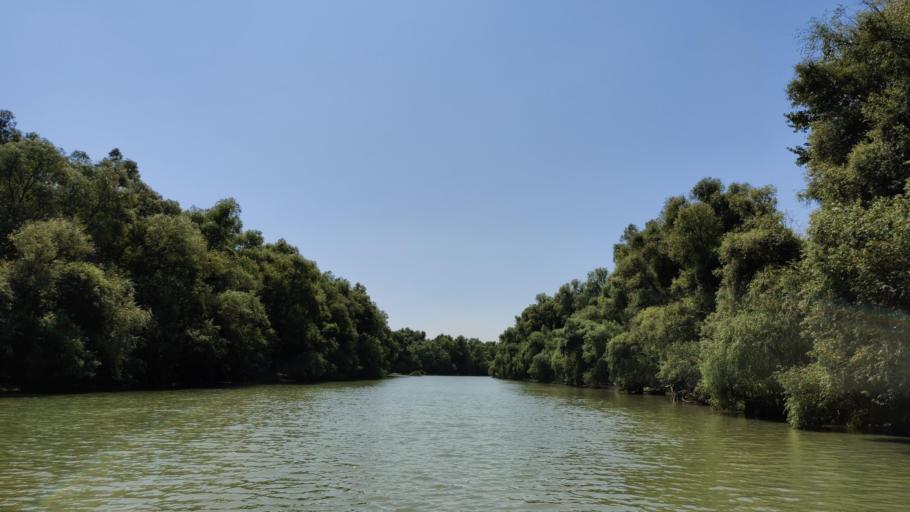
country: RO
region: Tulcea
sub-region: Comuna Pardina
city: Pardina
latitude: 45.2392
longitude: 28.9186
